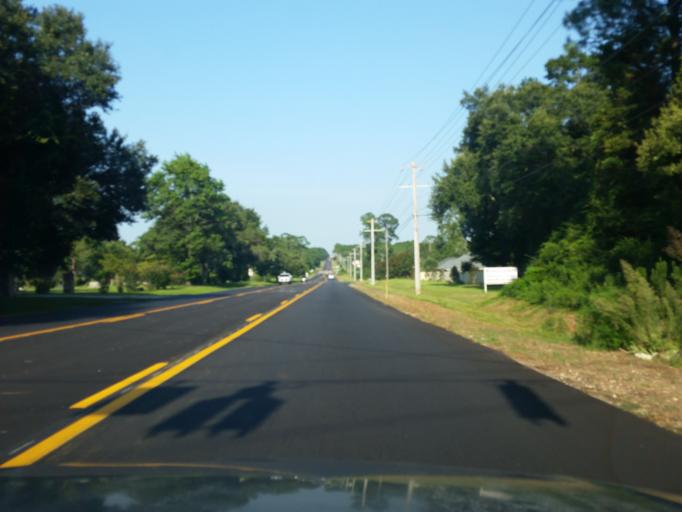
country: US
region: Alabama
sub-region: Baldwin County
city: Foley
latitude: 30.4066
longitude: -87.7423
